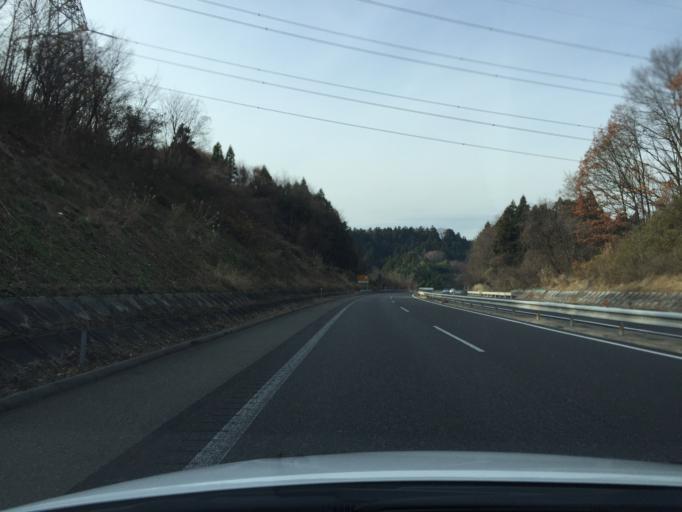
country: JP
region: Fukushima
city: Miharu
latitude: 37.4376
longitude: 140.4508
